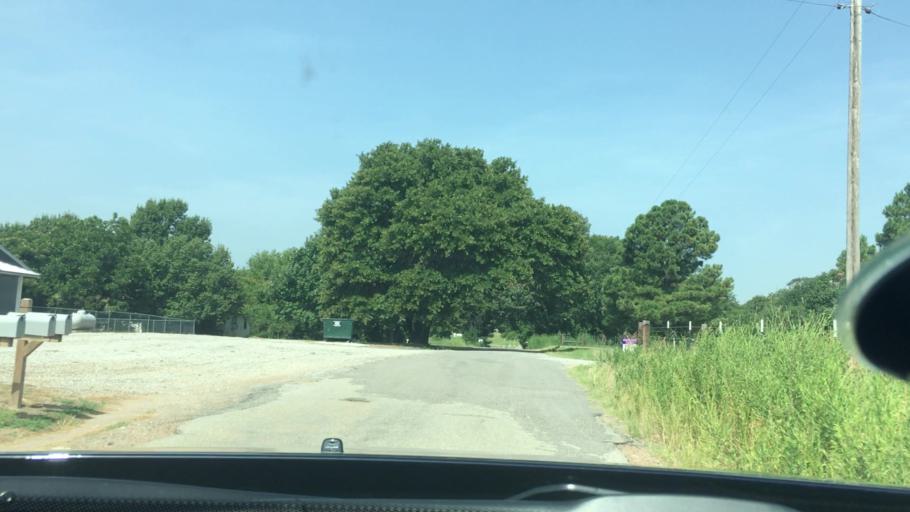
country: US
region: Oklahoma
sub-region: Atoka County
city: Atoka
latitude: 34.3603
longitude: -96.1698
